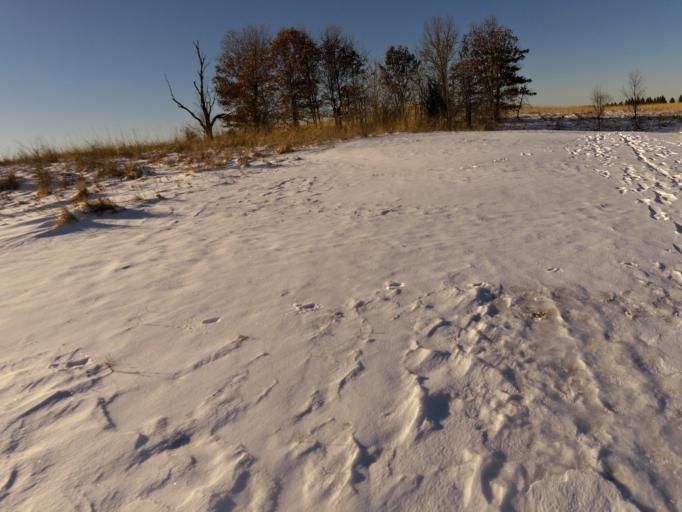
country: US
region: Minnesota
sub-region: Washington County
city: Lake Elmo
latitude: 44.9858
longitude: -92.9130
